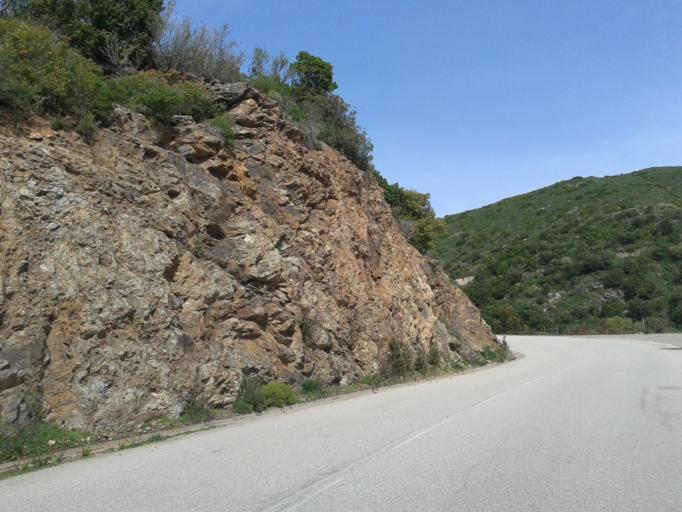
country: FR
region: Corsica
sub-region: Departement de la Haute-Corse
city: Monticello
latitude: 42.6563
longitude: 9.1151
